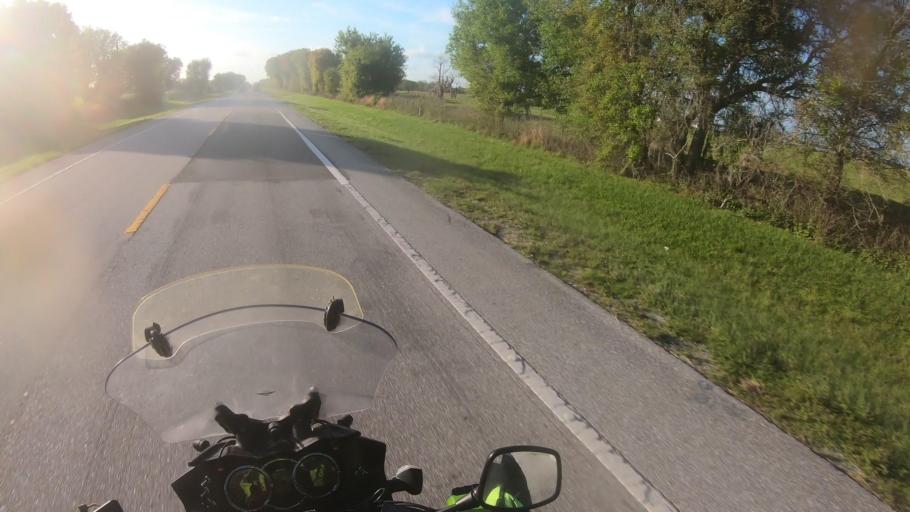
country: US
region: Florida
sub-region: DeSoto County
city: Arcadia
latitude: 27.2767
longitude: -82.0226
